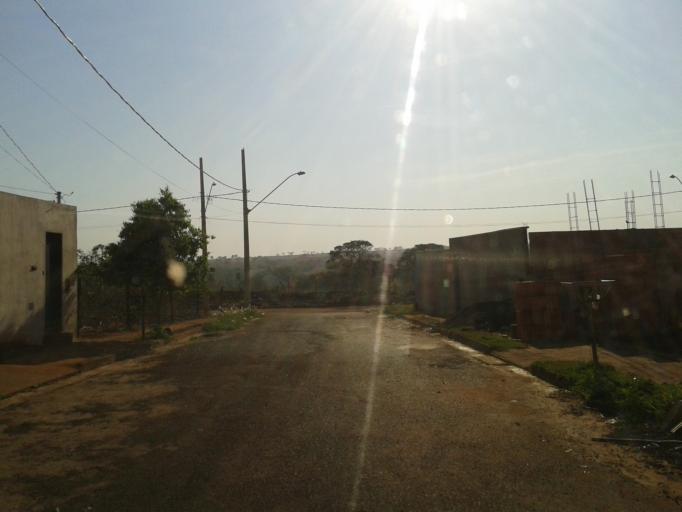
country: BR
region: Minas Gerais
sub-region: Ituiutaba
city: Ituiutaba
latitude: -18.9868
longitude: -49.4242
